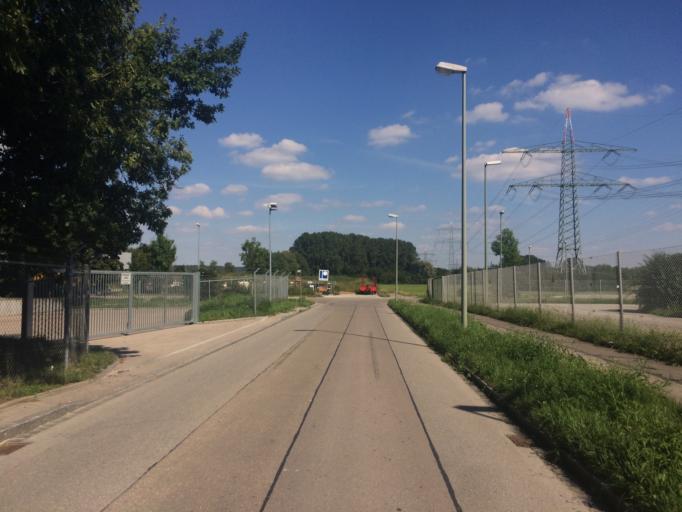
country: DE
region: Bavaria
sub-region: Swabia
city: Augsburg
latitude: 48.4021
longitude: 10.9364
